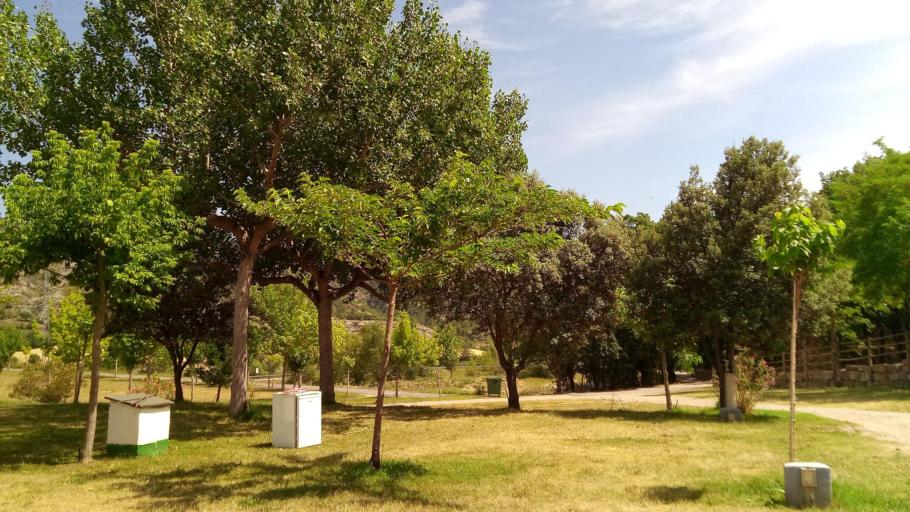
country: ES
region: Aragon
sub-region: Provincia de Huesca
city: Castigaleu
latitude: 42.3094
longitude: 0.5456
